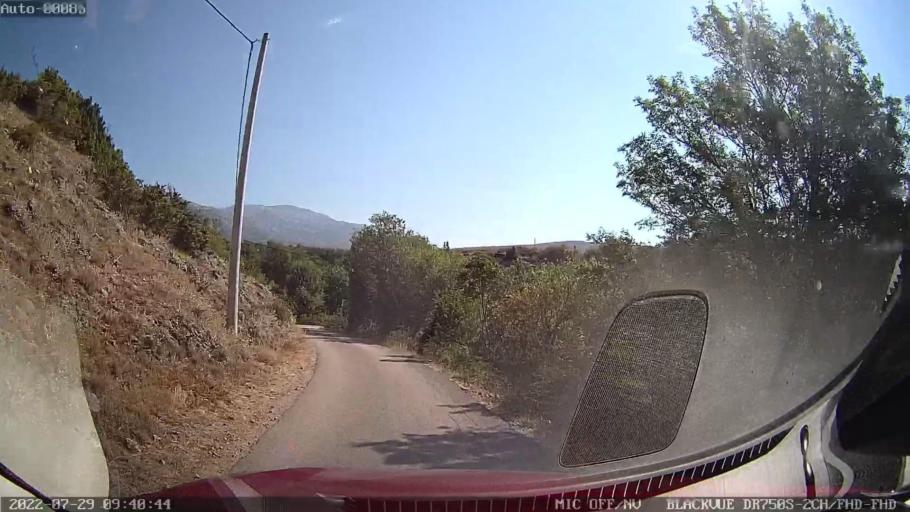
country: HR
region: Zadarska
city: Obrovac
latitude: 44.1955
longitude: 15.7665
